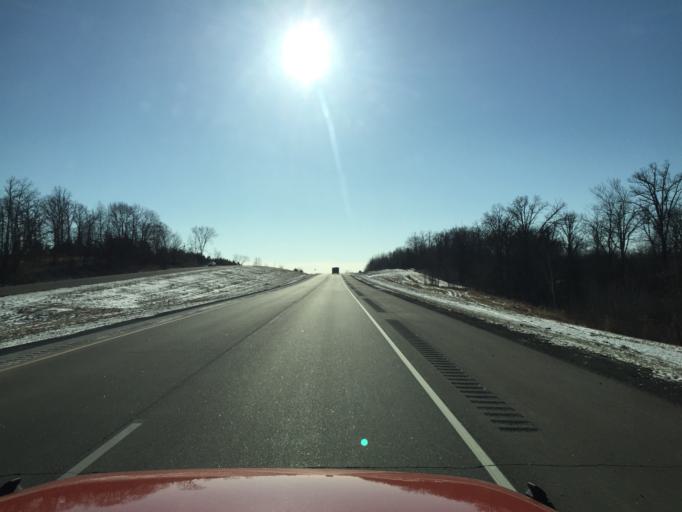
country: US
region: Minnesota
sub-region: Mille Lacs County
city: Milaca
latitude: 45.8137
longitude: -93.6553
